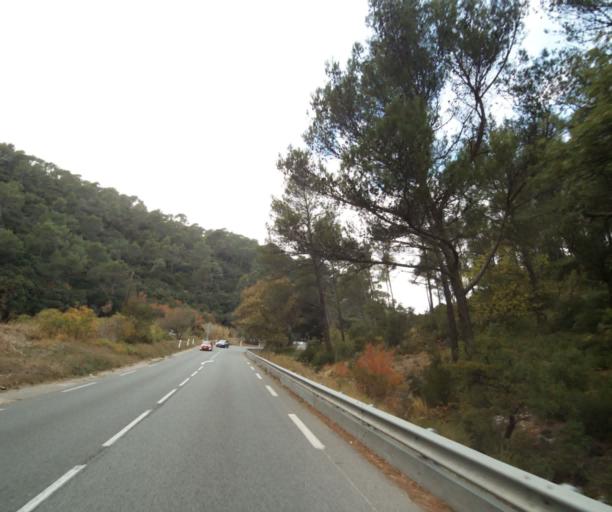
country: FR
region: Provence-Alpes-Cote d'Azur
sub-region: Departement des Bouches-du-Rhone
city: Gemenos
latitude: 43.2675
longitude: 5.6499
